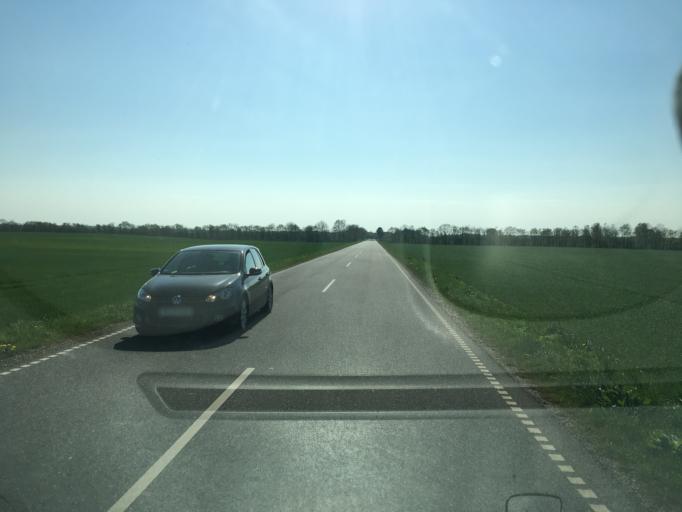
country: DK
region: South Denmark
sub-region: Haderslev Kommune
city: Vojens
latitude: 55.3037
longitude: 9.2639
